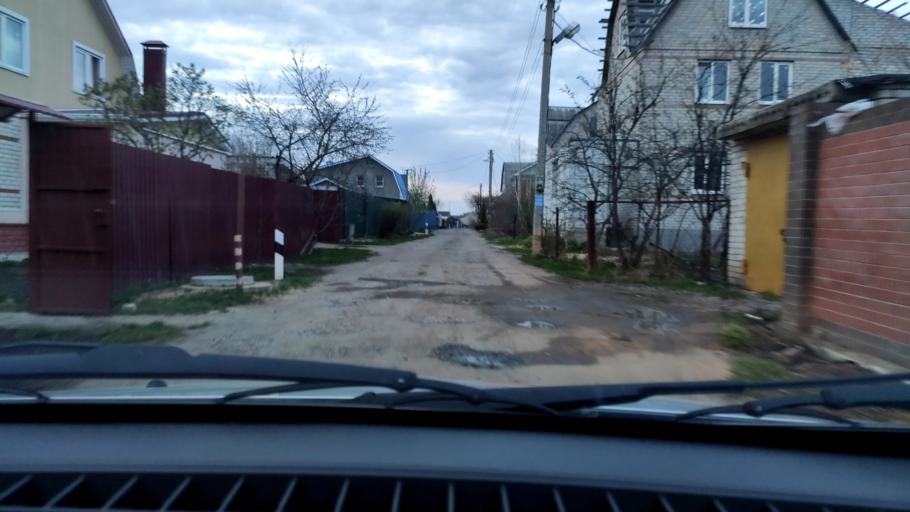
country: RU
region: Voronezj
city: Podgornoye
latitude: 51.7962
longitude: 39.2197
